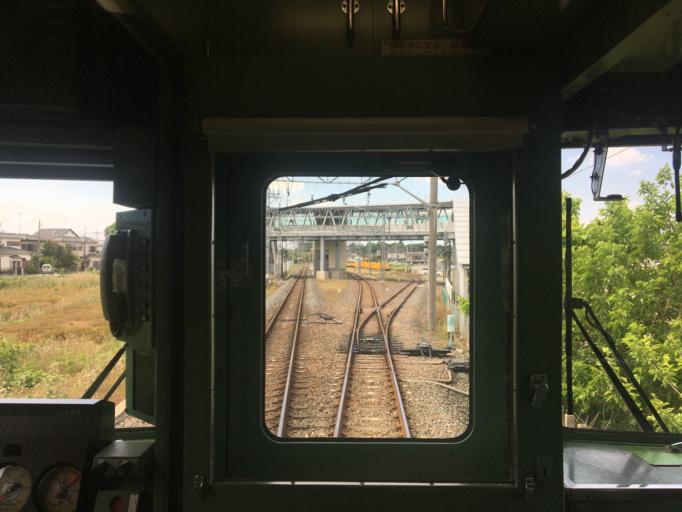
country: JP
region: Saitama
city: Yorii
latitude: 36.1066
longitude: 139.2345
